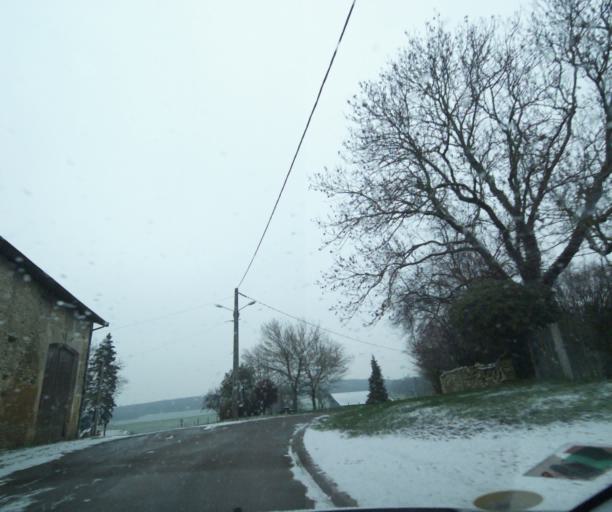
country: FR
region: Champagne-Ardenne
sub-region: Departement de la Haute-Marne
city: Wassy
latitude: 48.4605
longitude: 5.0306
